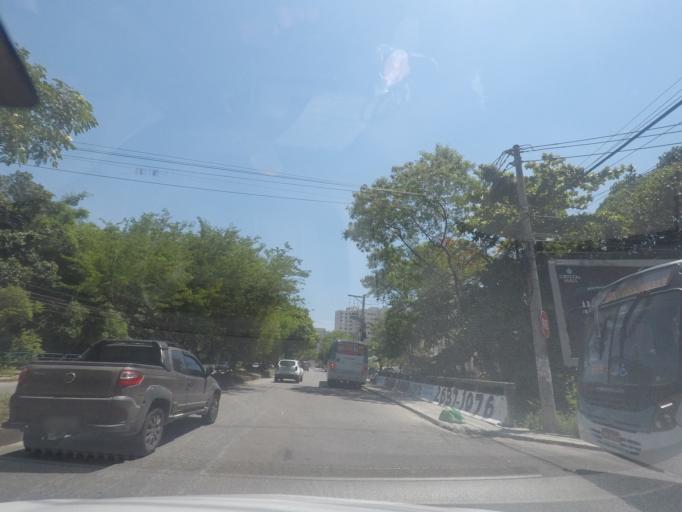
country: BR
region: Rio de Janeiro
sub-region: Nilopolis
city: Nilopolis
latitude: -22.9751
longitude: -43.4148
